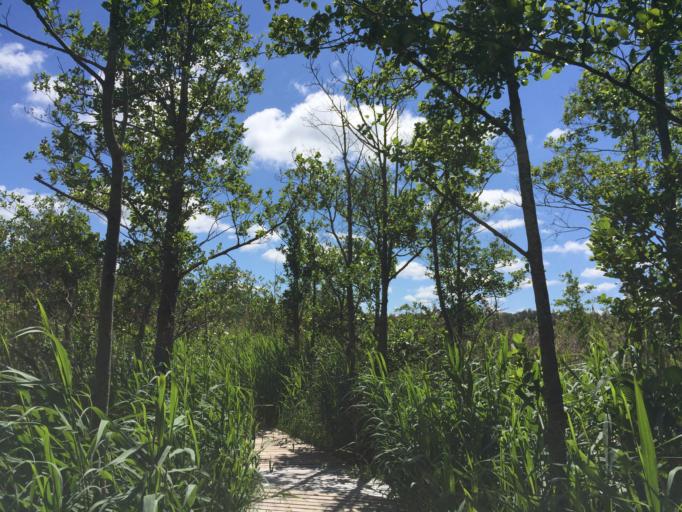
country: LV
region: Ventspils
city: Ventspils
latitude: 57.4436
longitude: 21.6331
